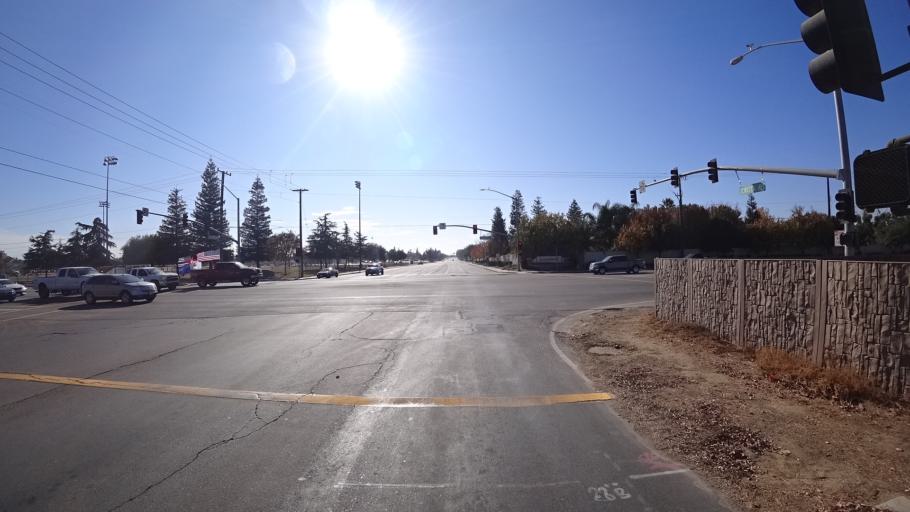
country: US
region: California
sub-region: Kern County
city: Rosedale
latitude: 35.3692
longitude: -119.1280
